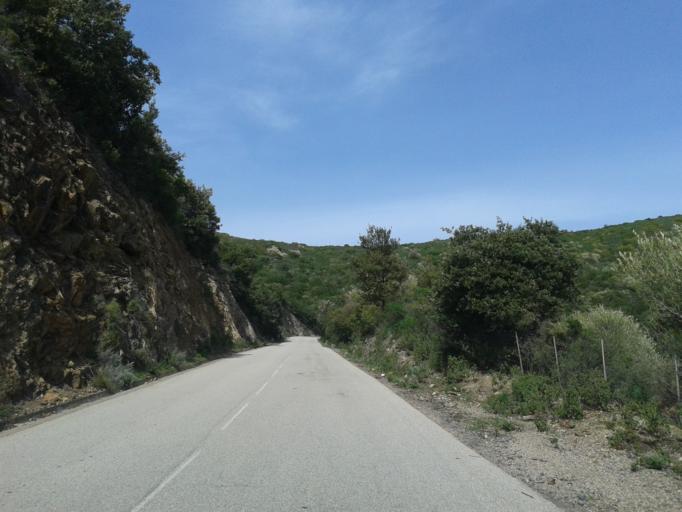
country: FR
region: Corsica
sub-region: Departement de la Haute-Corse
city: Monticello
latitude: 42.6569
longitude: 9.1153
